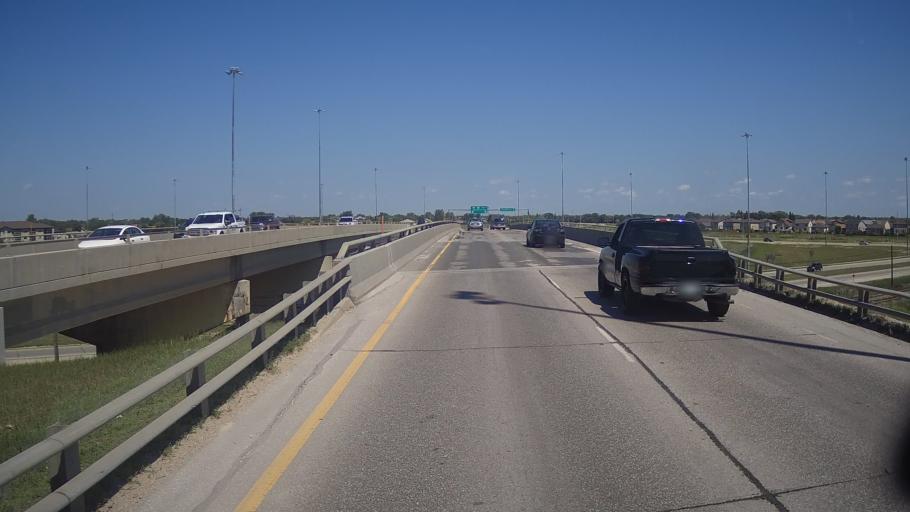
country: CA
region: Manitoba
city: Winnipeg
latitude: 49.9099
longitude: -97.0569
